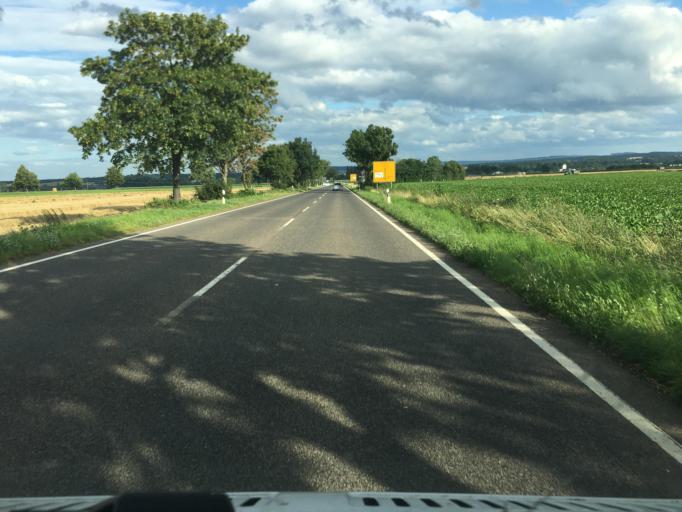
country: DE
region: North Rhine-Westphalia
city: Zulpich
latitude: 50.6793
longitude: 6.6392
